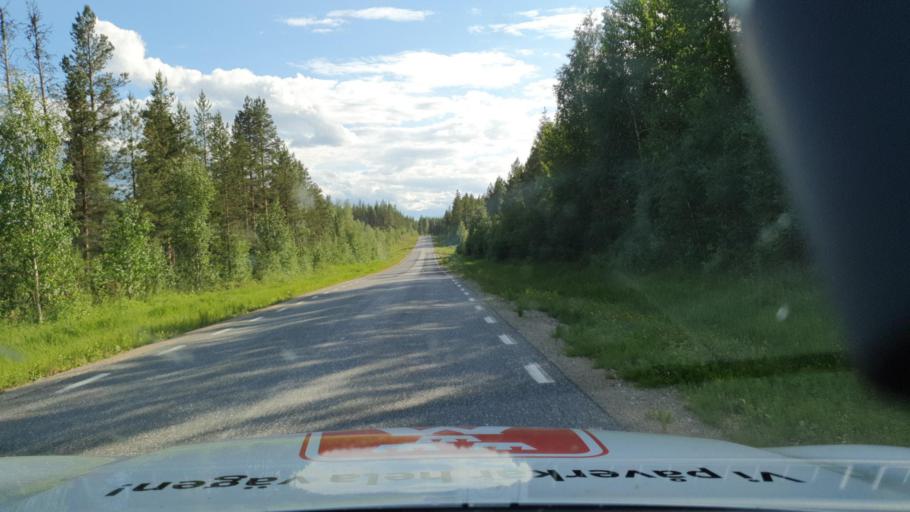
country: SE
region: Vaesterbotten
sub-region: Vindelns Kommun
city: Vindeln
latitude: 64.5345
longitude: 19.8910
